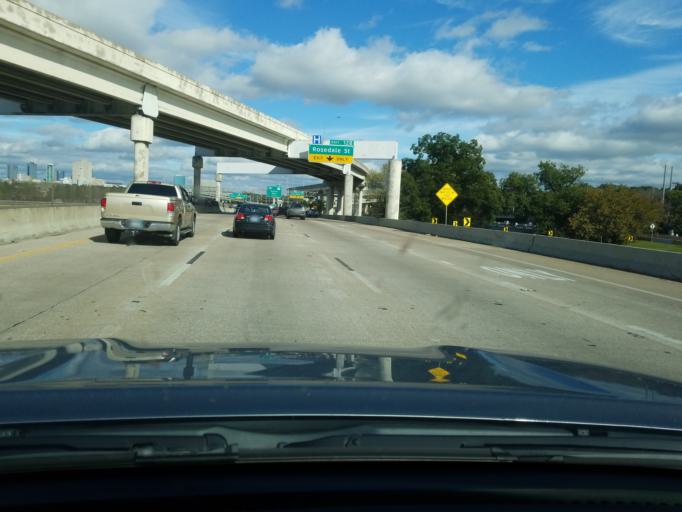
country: US
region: Texas
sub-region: Tarrant County
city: Fort Worth
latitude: 32.7335
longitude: -97.3615
